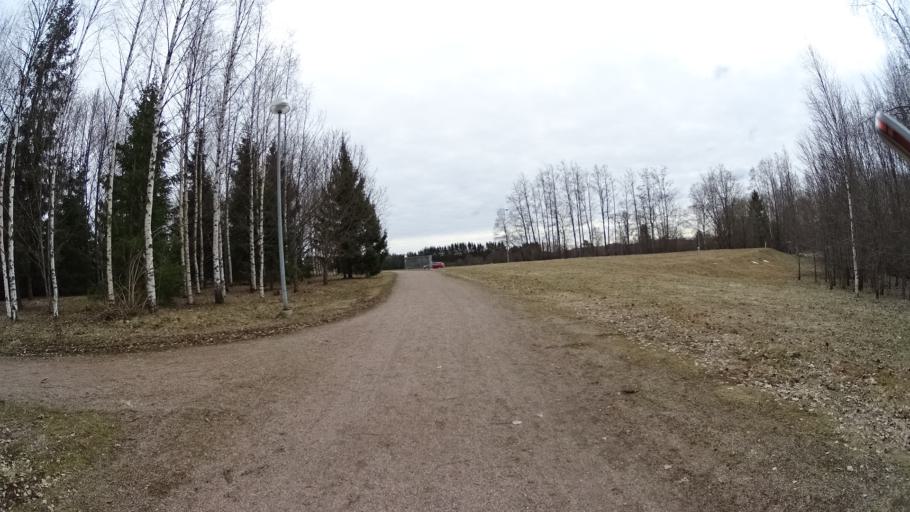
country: FI
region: Uusimaa
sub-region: Helsinki
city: Vantaa
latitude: 60.2860
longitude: 24.9434
